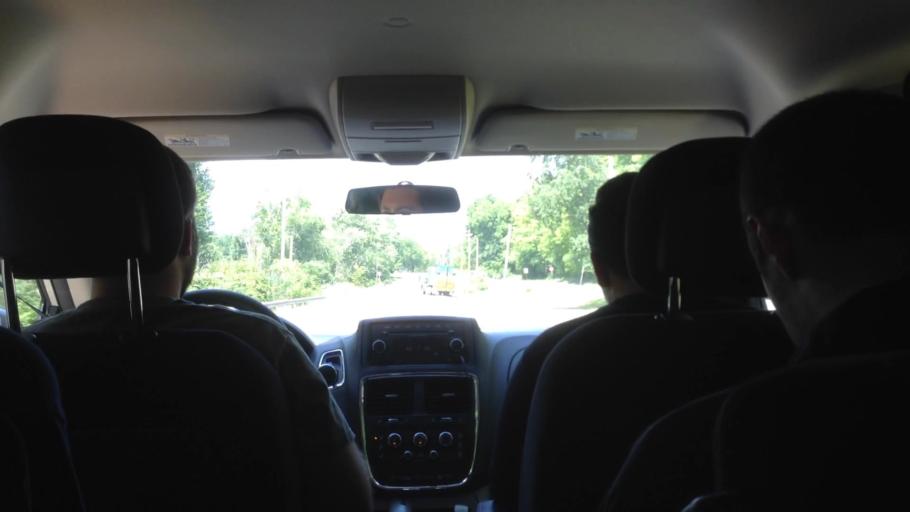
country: US
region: New York
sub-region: Dutchess County
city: Red Hook
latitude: 42.0336
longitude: -73.8472
